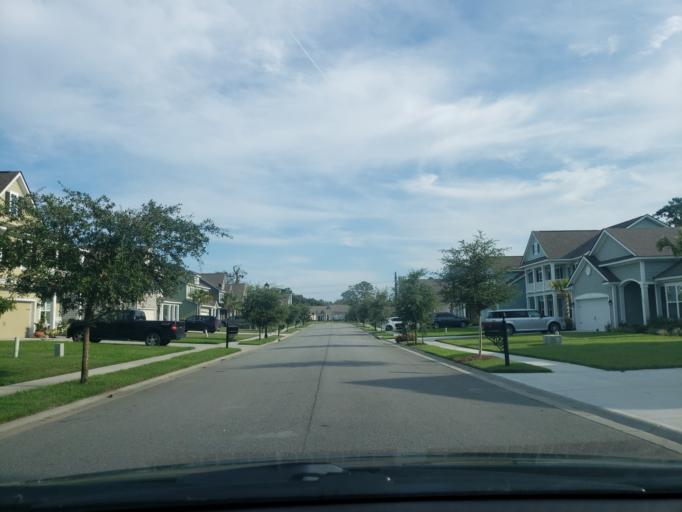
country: US
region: Georgia
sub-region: Chatham County
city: Montgomery
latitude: 31.9562
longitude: -81.1559
